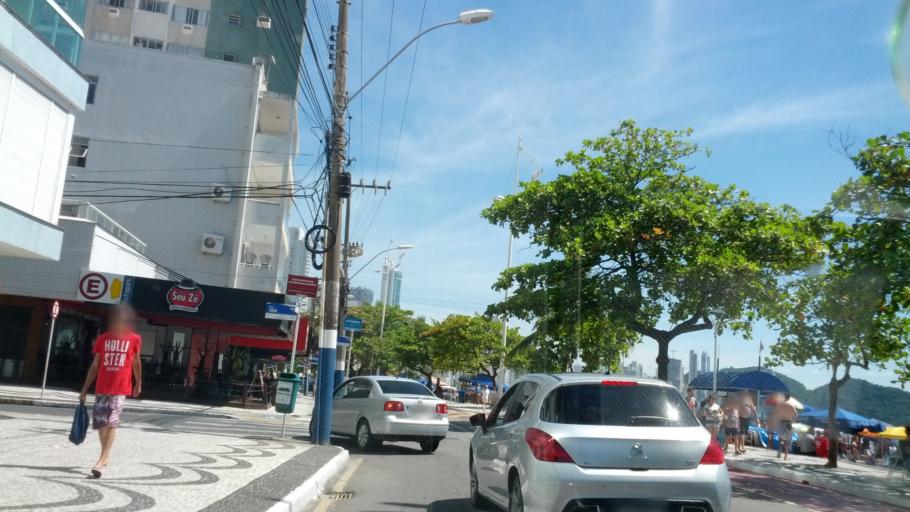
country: BR
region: Santa Catarina
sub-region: Balneario Camboriu
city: Balneario Camboriu
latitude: -26.9899
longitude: -48.6296
